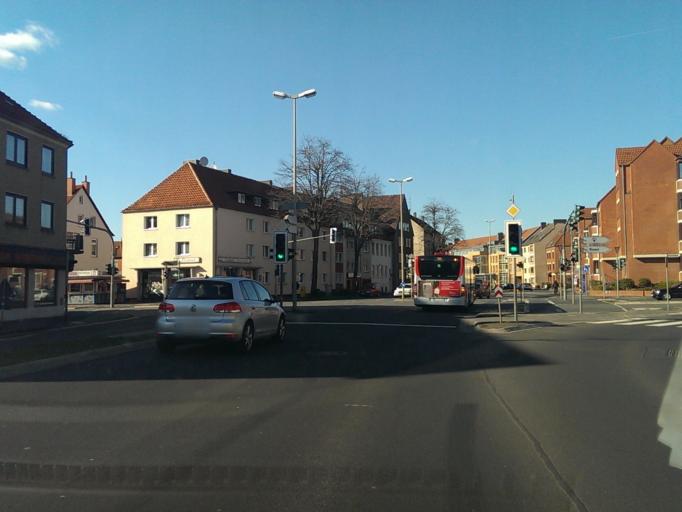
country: DE
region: Lower Saxony
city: Hildesheim
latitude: 52.1487
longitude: 9.9383
